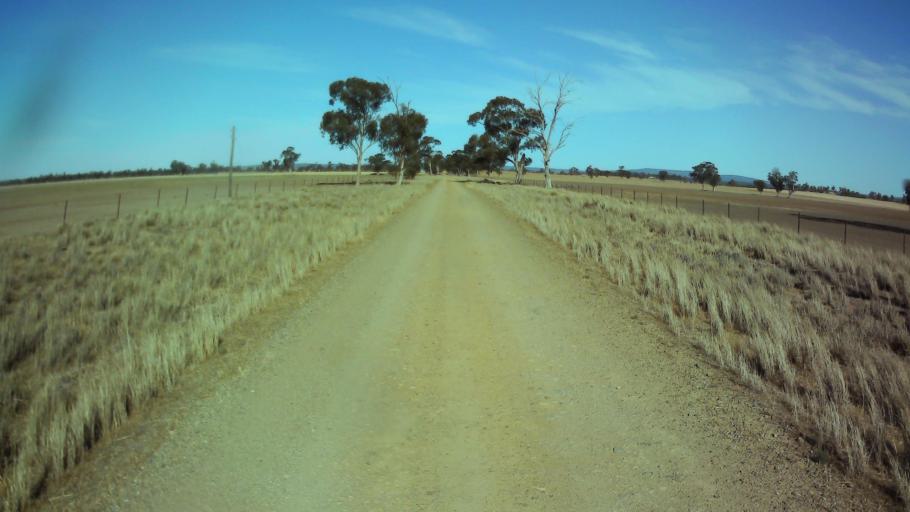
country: AU
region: New South Wales
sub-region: Weddin
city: Grenfell
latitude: -33.6593
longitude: 148.1058
